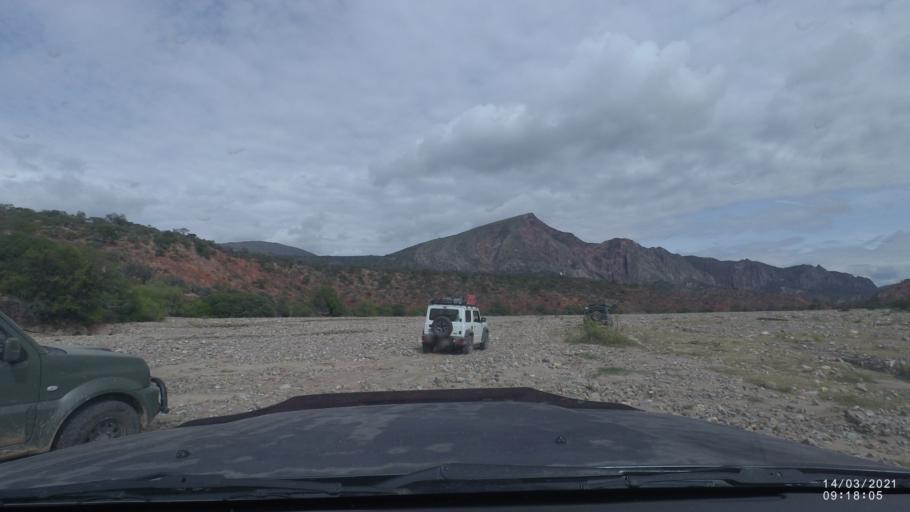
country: BO
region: Cochabamba
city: Cliza
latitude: -17.9489
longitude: -65.8548
